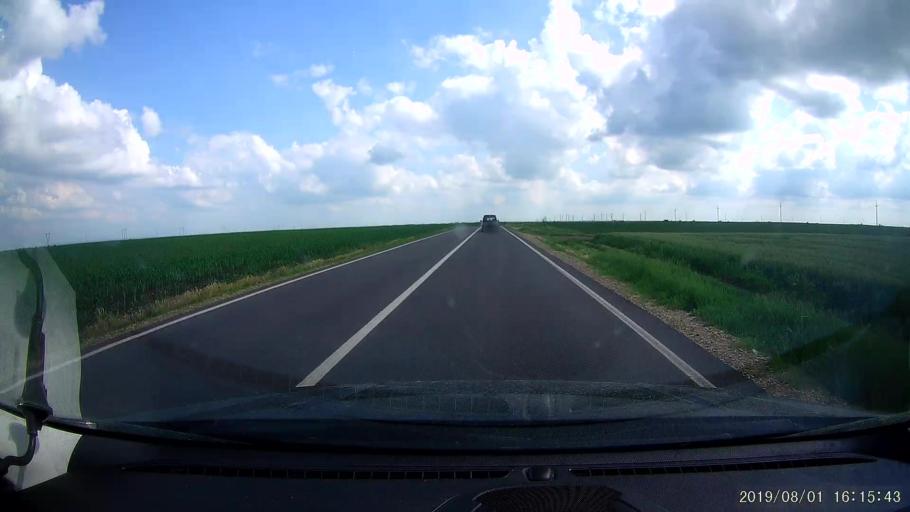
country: RO
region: Calarasi
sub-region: Comuna Stefan Voda
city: Stefan Voda
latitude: 44.3329
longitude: 27.3602
